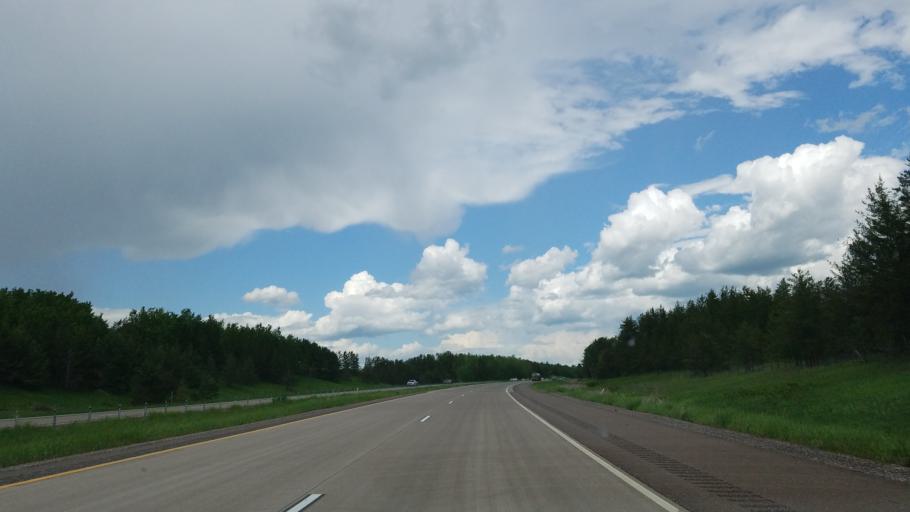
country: US
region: Minnesota
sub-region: Carlton County
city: Moose Lake
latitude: 46.4839
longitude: -92.7079
